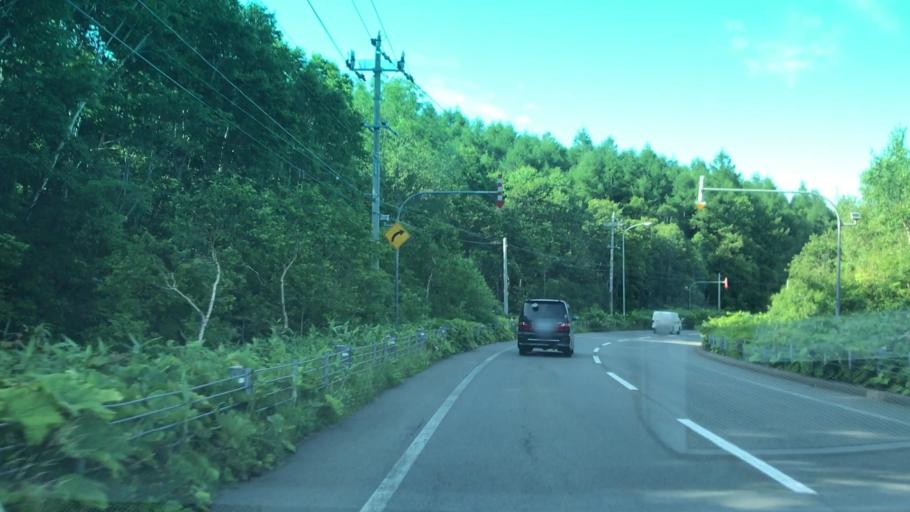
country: JP
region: Hokkaido
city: Otaru
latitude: 43.1087
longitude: 141.0050
